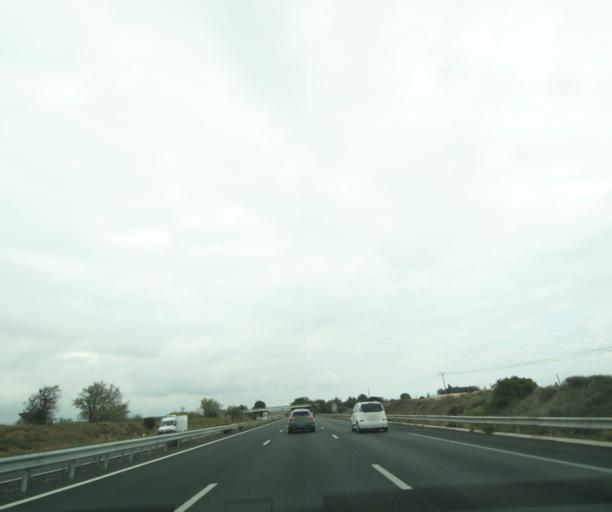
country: FR
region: Languedoc-Roussillon
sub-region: Departement de l'Herault
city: Pinet
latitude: 43.4091
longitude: 3.5022
